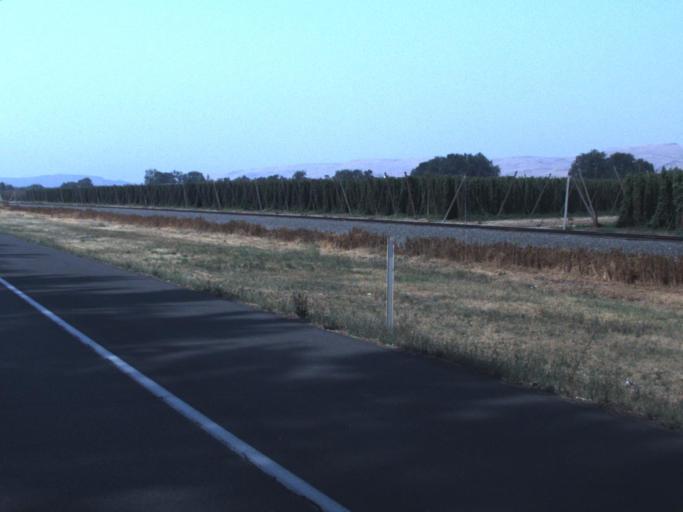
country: US
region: Washington
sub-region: Yakima County
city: Terrace Heights
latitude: 46.5708
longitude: -120.4257
